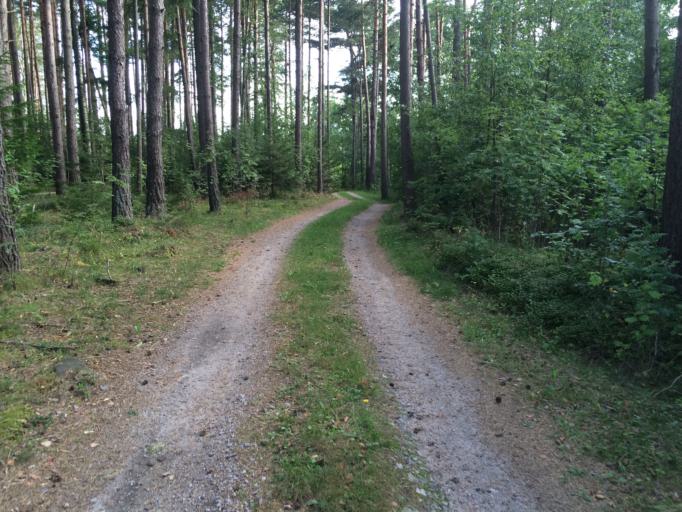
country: NO
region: Ostfold
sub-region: Hvaler
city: Skjaerhalden
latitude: 59.0367
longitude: 11.0096
